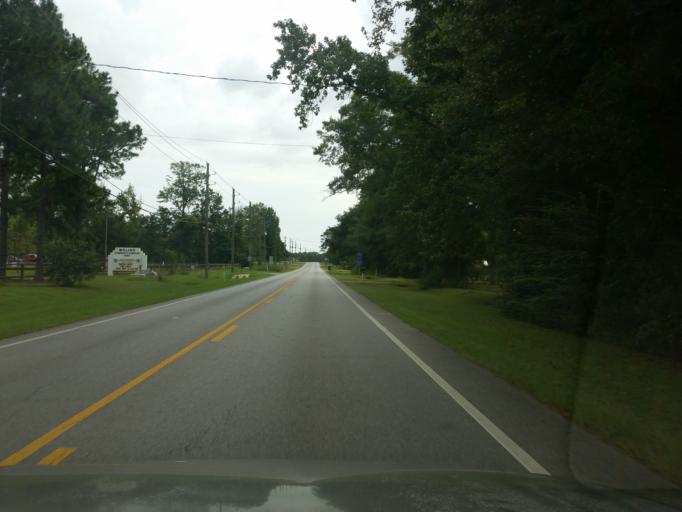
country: US
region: Florida
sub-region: Escambia County
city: Molino
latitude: 30.7163
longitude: -87.3380
